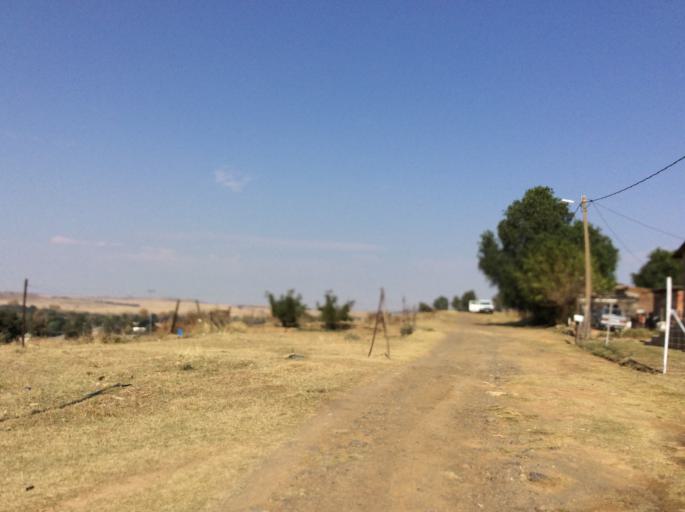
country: LS
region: Mafeteng
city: Mafeteng
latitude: -29.7209
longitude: 27.0347
